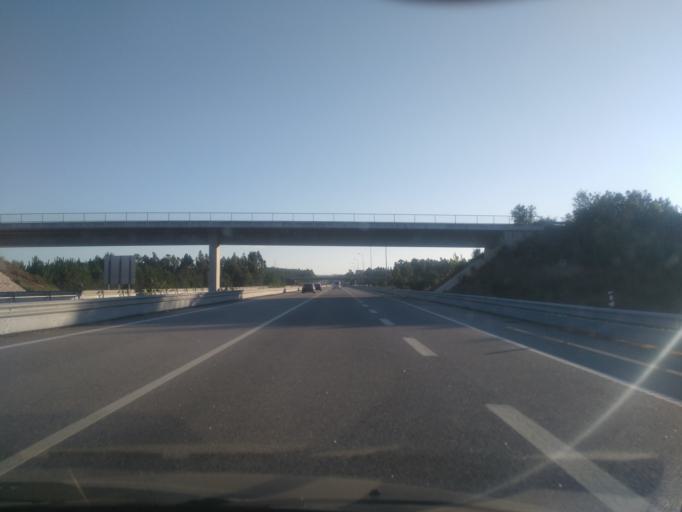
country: PT
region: Coimbra
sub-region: Figueira da Foz
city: Alhadas
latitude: 40.2248
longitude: -8.7950
